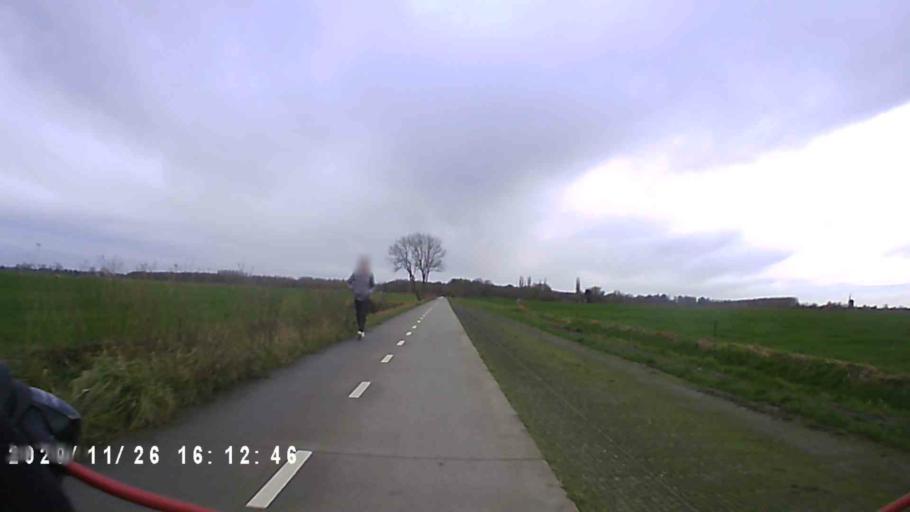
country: NL
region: Groningen
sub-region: Gemeente Groningen
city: Oosterpark
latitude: 53.2487
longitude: 6.6444
